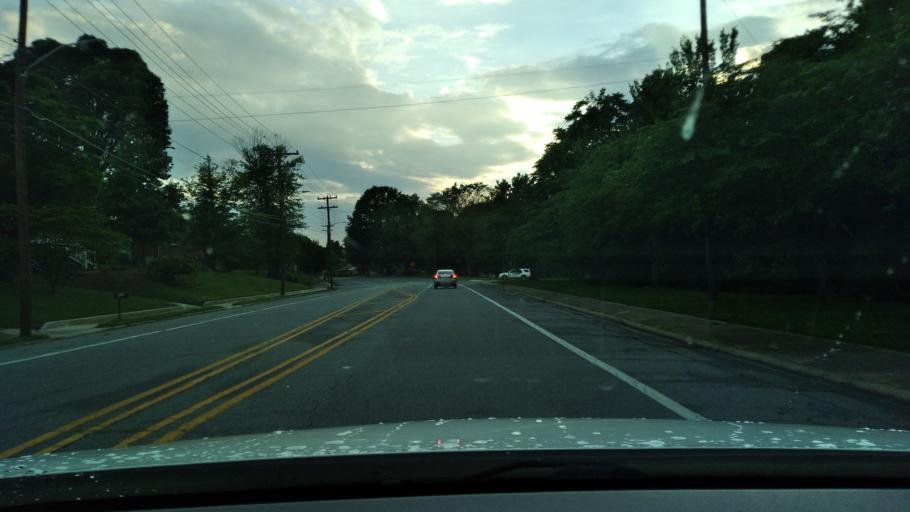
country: US
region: North Carolina
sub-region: Guilford County
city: Greensboro
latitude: 36.0546
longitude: -79.7758
